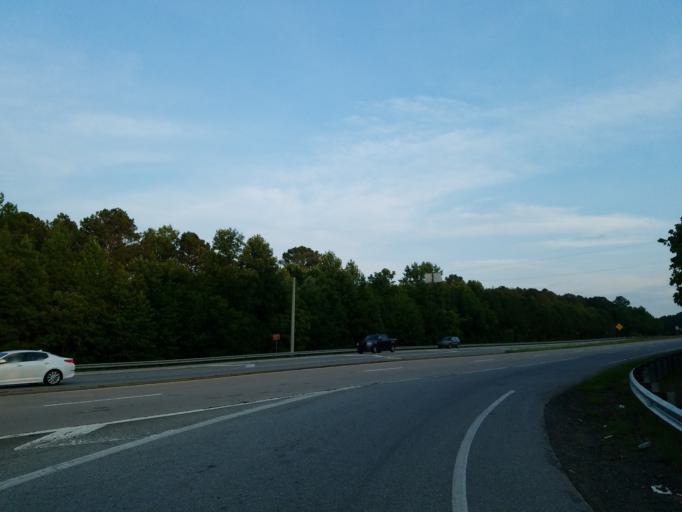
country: US
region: Georgia
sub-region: Pickens County
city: Jasper
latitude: 34.5176
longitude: -84.5192
